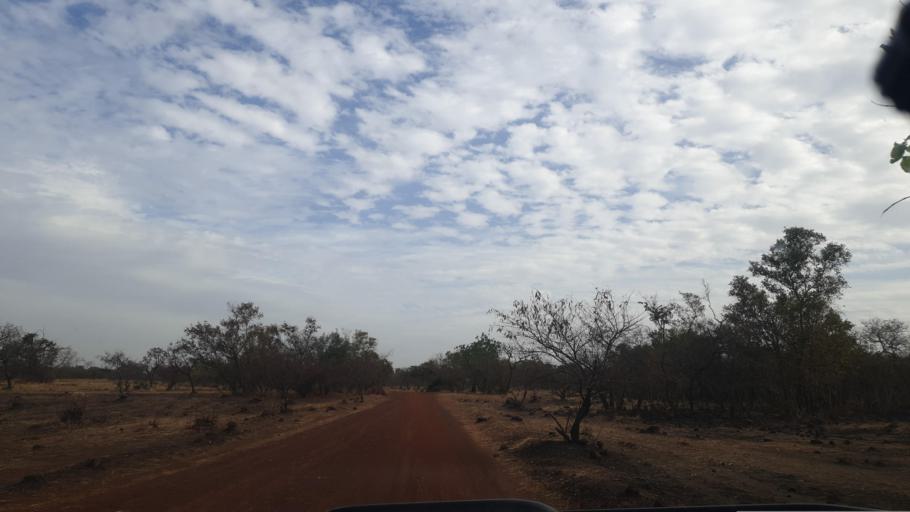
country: ML
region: Sikasso
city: Yanfolila
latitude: 11.3955
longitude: -8.0196
